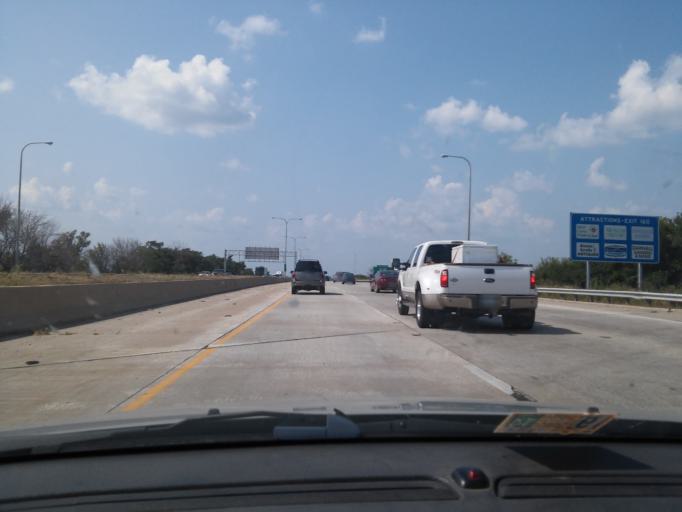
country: US
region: Illinois
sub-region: McLean County
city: Bloomington
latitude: 40.4527
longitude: -89.0240
